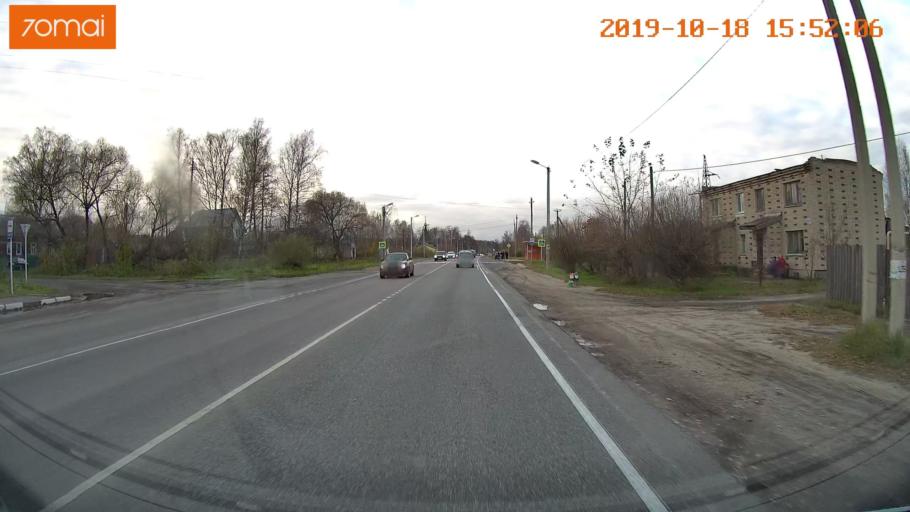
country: RU
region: Vladimir
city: Kommunar
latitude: 56.0452
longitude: 40.5398
